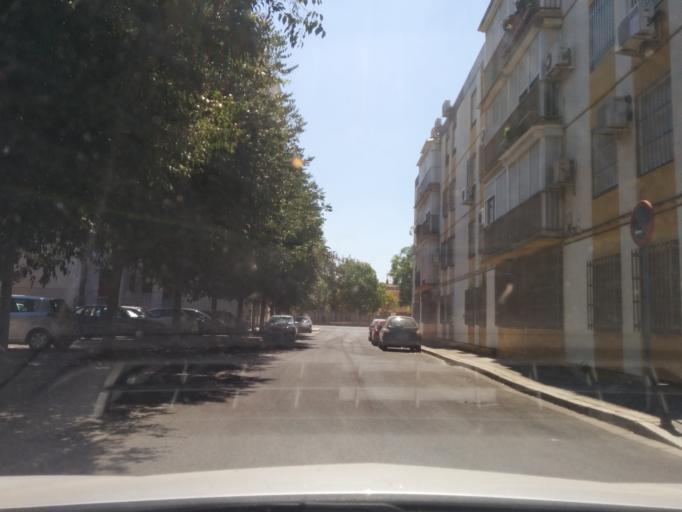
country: ES
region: Andalusia
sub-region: Provincia de Sevilla
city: Sevilla
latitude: 37.3639
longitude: -5.9699
